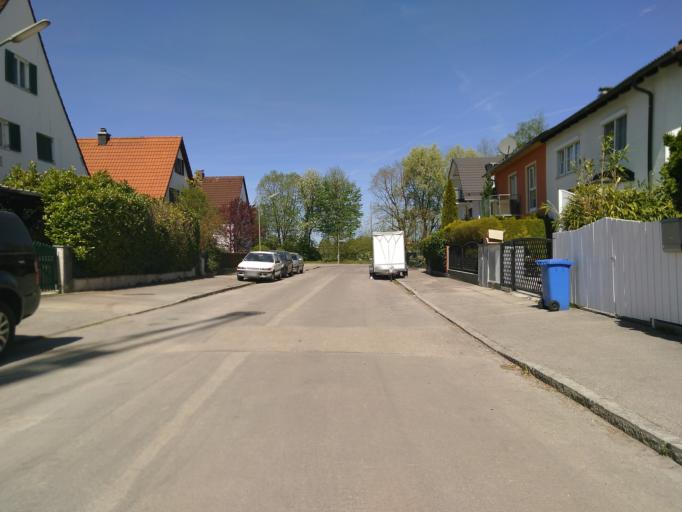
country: DE
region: Bavaria
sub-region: Upper Bavaria
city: Unterhaching
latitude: 48.0968
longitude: 11.6048
